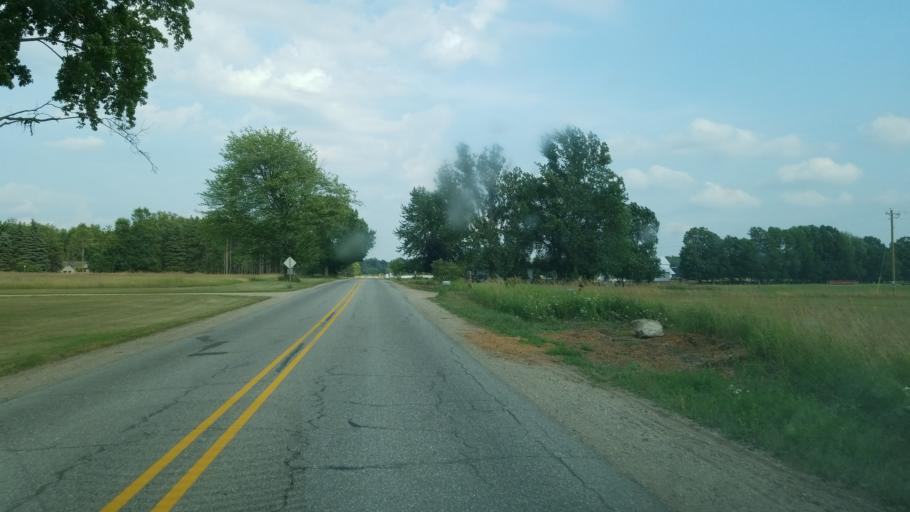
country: US
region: Michigan
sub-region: Mecosta County
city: Canadian Lakes
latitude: 43.5419
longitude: -85.3305
